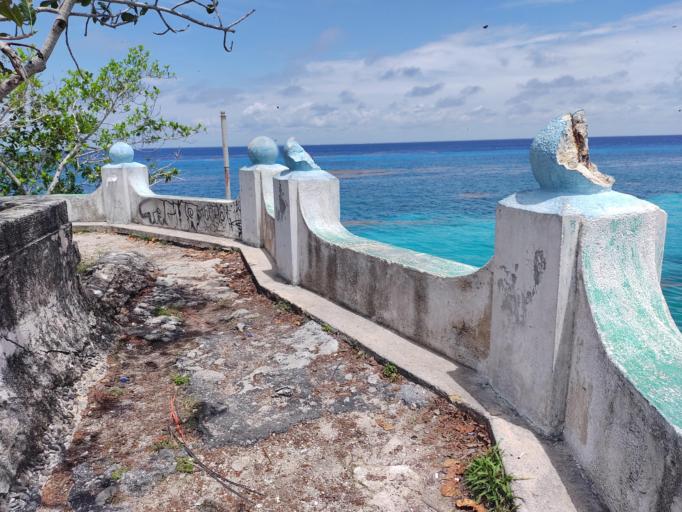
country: MX
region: Quintana Roo
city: San Miguel de Cozumel
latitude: 20.5273
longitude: -86.9408
